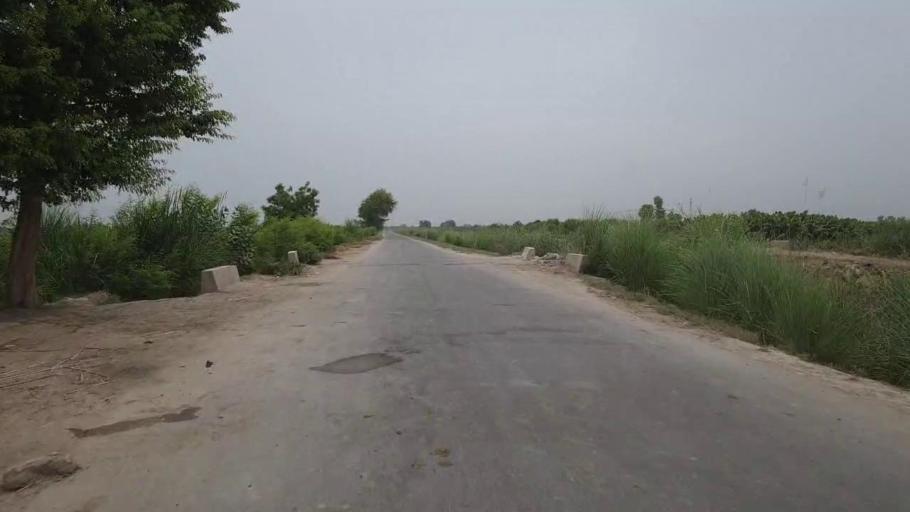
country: PK
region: Sindh
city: Bandhi
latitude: 26.5560
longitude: 68.2085
